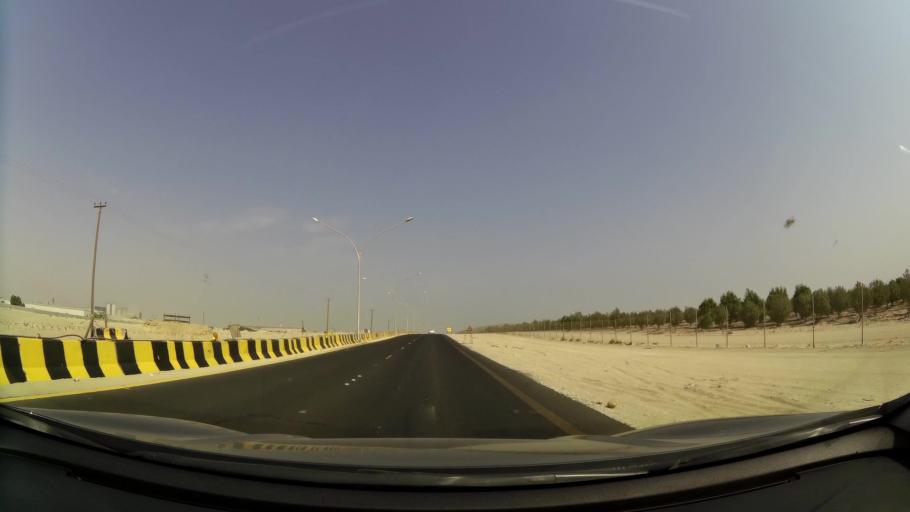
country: KW
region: Al Ahmadi
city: Al Fahahil
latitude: 28.9779
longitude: 48.1321
